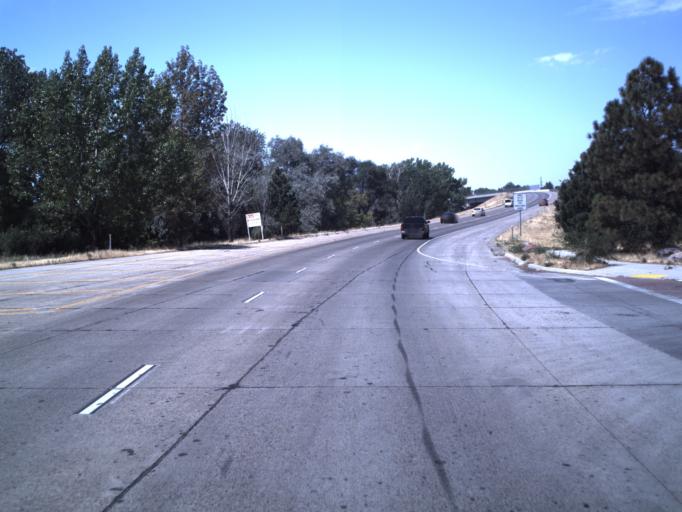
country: US
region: Utah
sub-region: Weber County
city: Ogden
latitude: 41.2310
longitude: -111.9824
